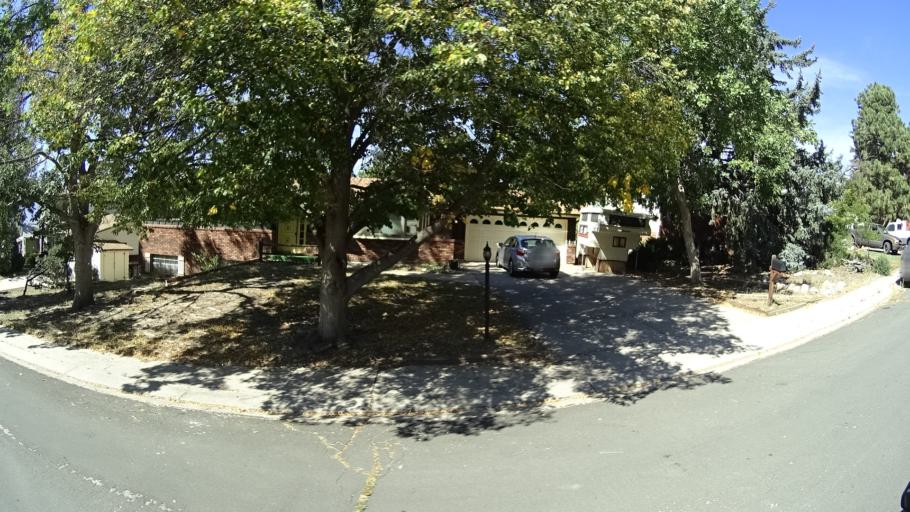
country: US
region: Colorado
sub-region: El Paso County
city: Cimarron Hills
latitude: 38.9102
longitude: -104.7682
